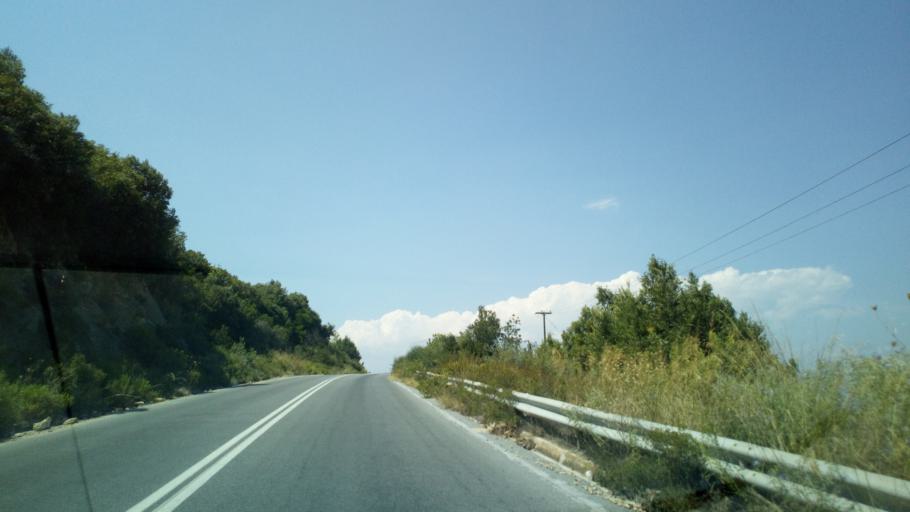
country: GR
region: Central Macedonia
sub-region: Nomos Chalkidikis
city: Sarti
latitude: 40.1562
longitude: 23.9084
